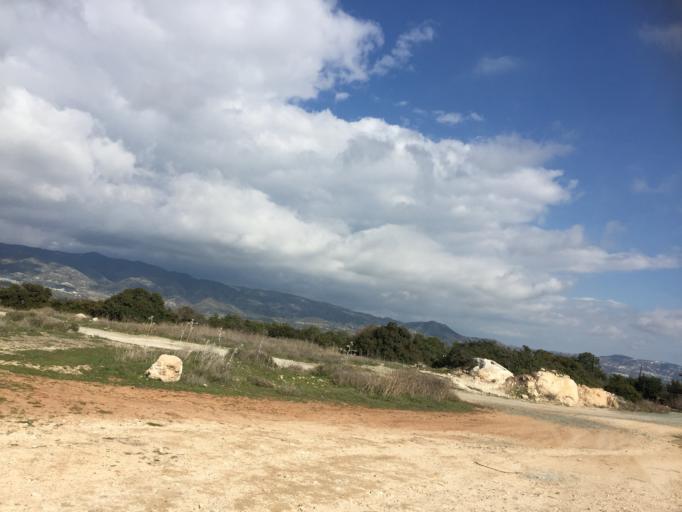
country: CY
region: Larnaka
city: Agios Tychon
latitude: 34.7446
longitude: 33.1369
